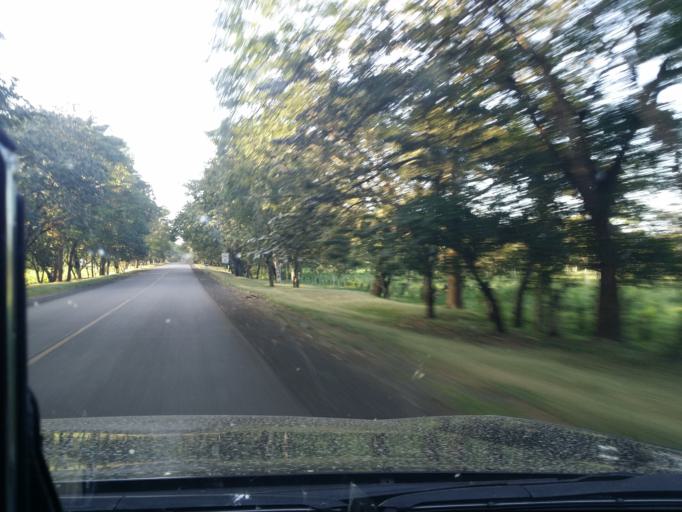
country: NI
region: Rio San Juan
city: San Miguelito
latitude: 11.4114
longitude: -84.8373
